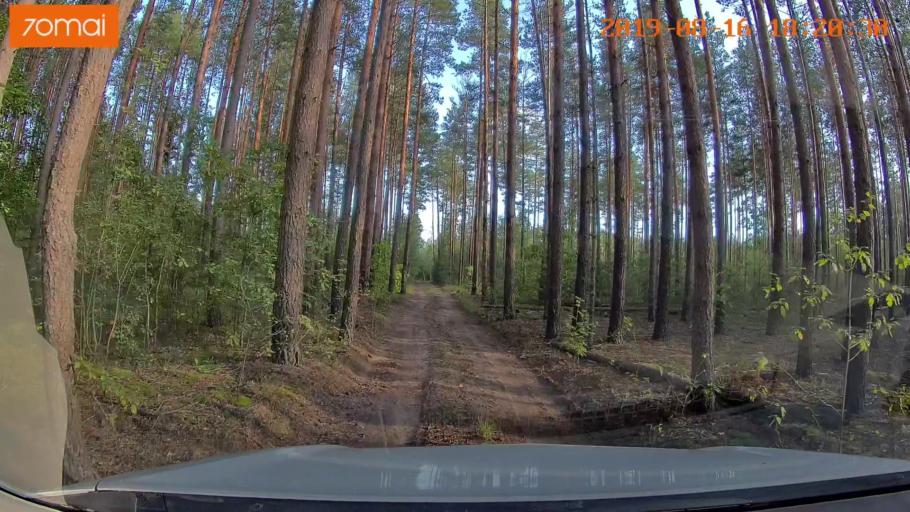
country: BY
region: Mogilev
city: Asipovichy
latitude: 53.2075
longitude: 28.6333
